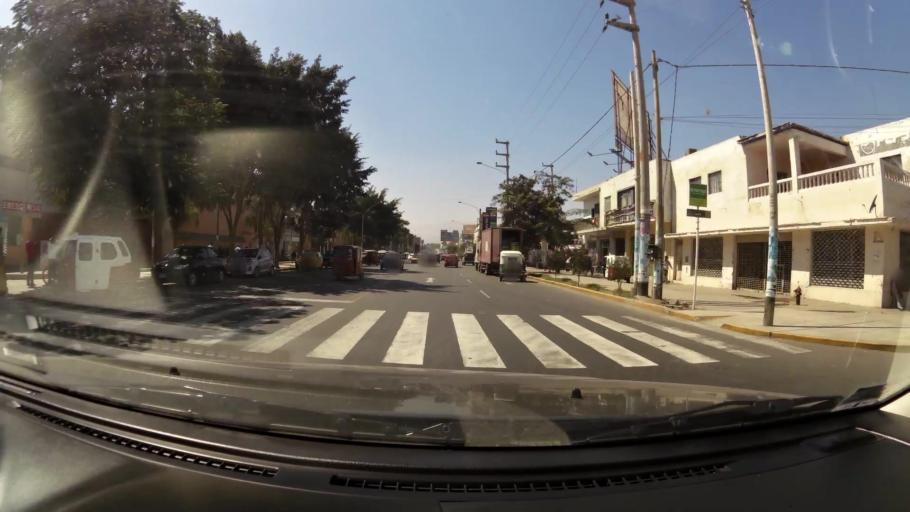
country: PE
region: Ica
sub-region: Provincia de Ica
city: Ica
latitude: -14.0661
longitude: -75.7385
